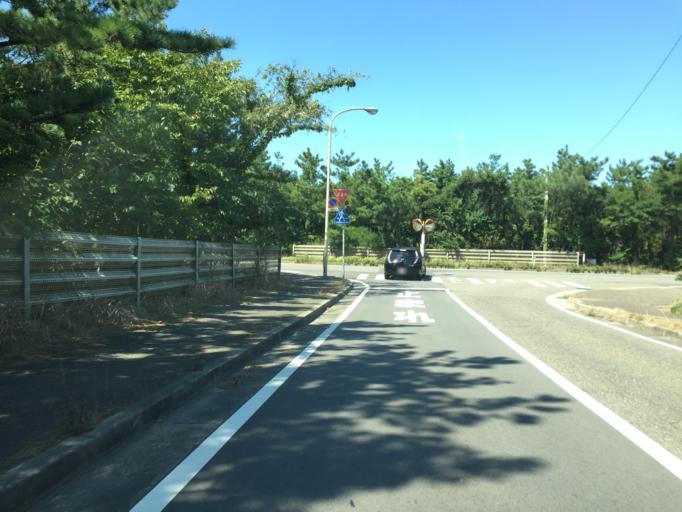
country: JP
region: Niigata
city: Niigata-shi
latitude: 37.9016
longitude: 138.9916
